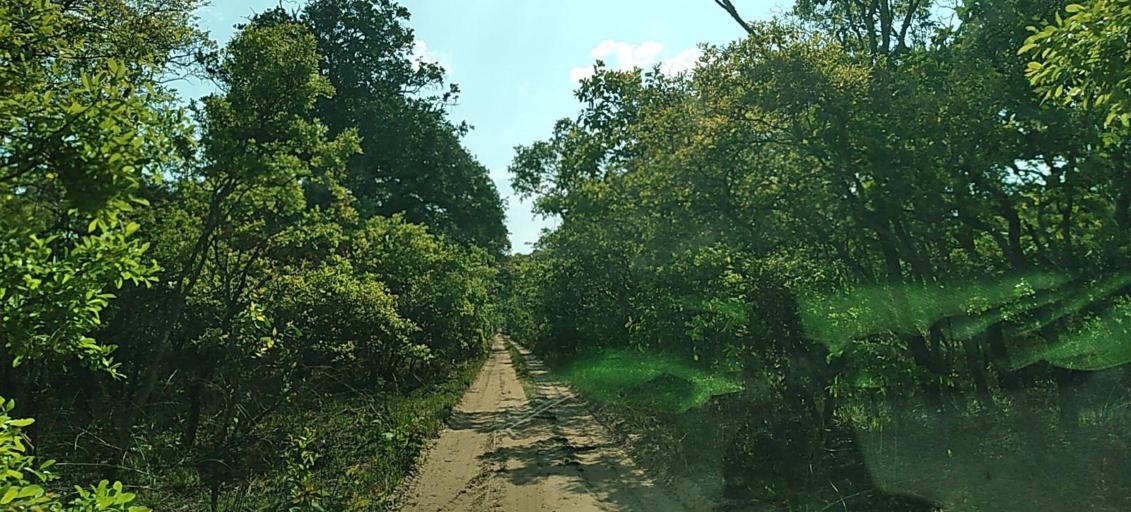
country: ZM
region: North-Western
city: Mwinilunga
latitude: -11.3013
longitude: 24.8447
